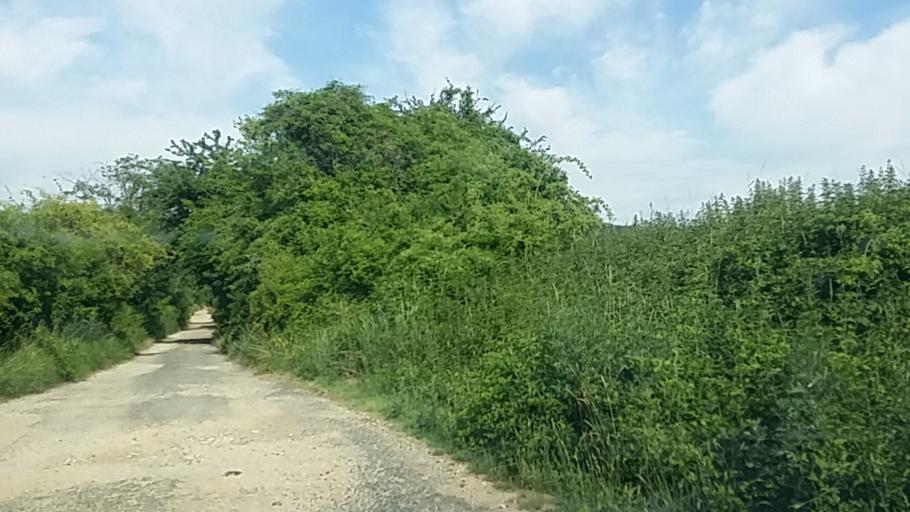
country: HU
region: Komarom-Esztergom
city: Bajna
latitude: 47.6927
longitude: 18.5553
